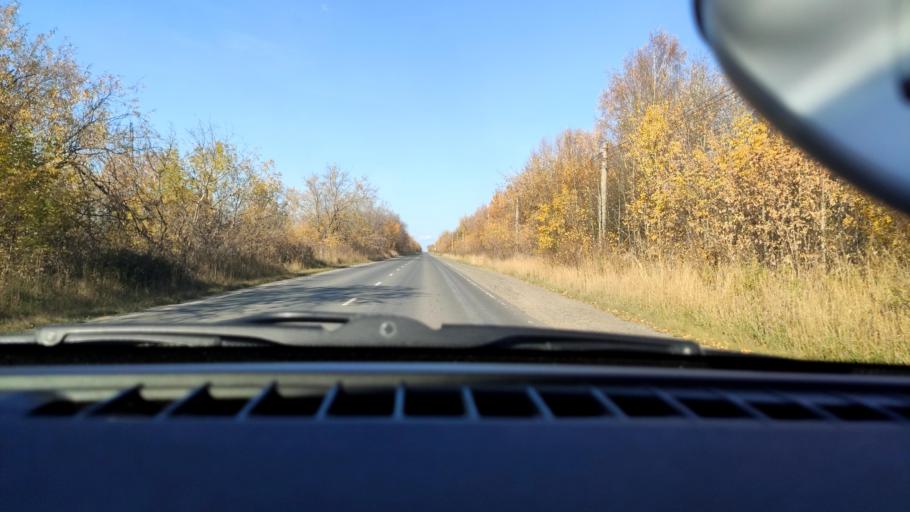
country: RU
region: Perm
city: Gamovo
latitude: 57.8990
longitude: 56.1798
